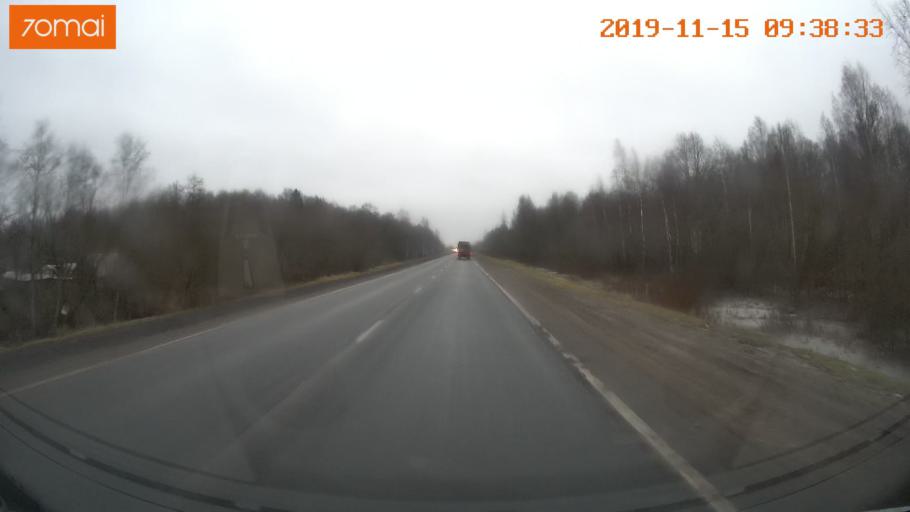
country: RU
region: Vologda
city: Sheksna
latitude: 59.2309
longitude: 38.4579
